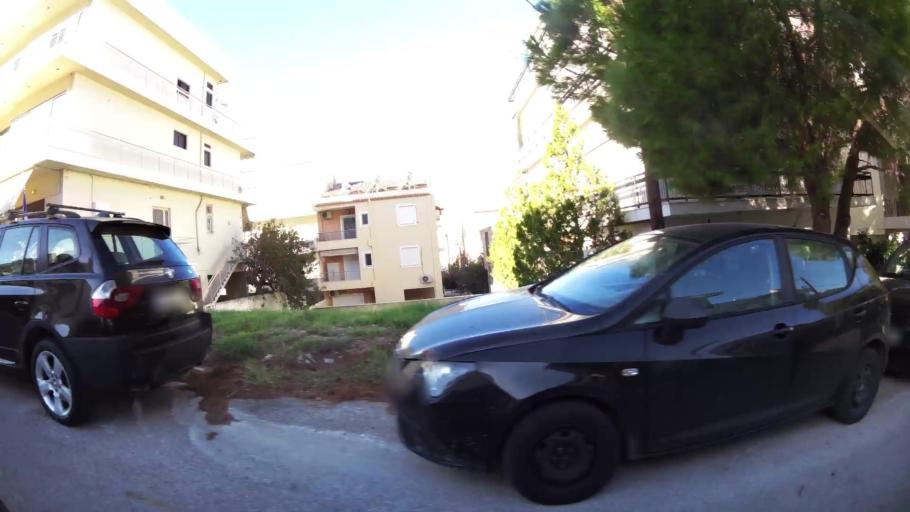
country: GR
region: Attica
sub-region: Nomarchia Athinas
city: Glyfada
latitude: 37.8775
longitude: 23.7714
